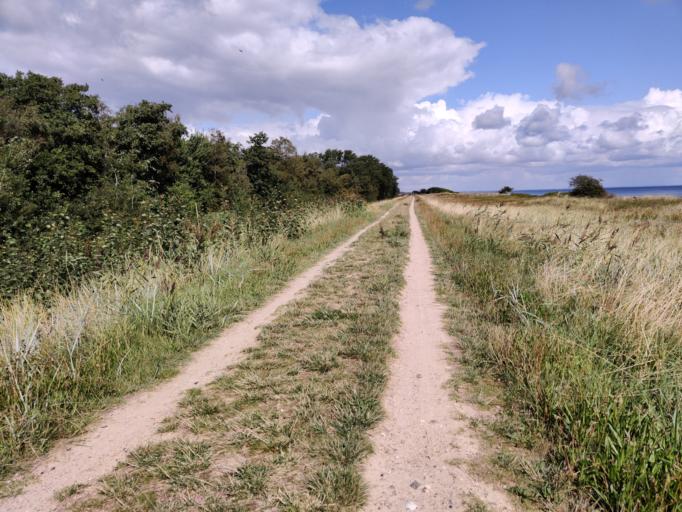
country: DK
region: Zealand
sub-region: Guldborgsund Kommune
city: Nykobing Falster
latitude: 54.5868
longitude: 11.9710
